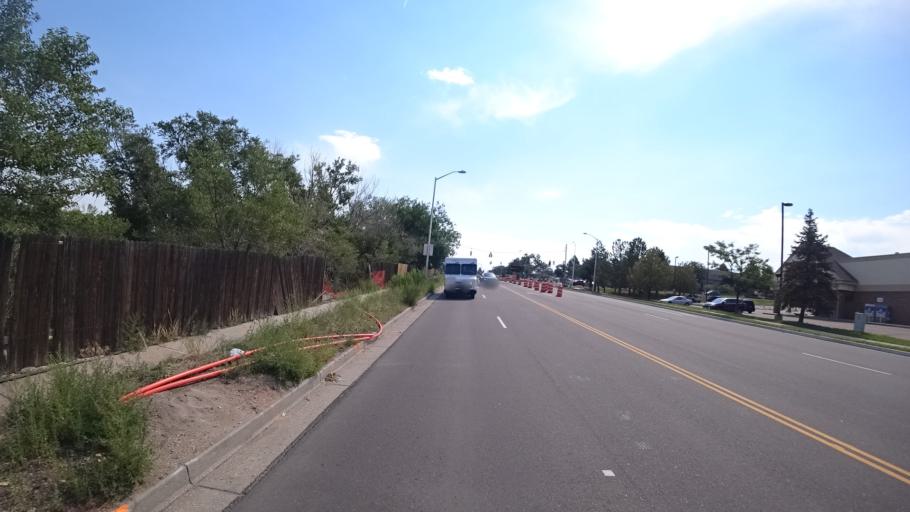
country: US
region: Colorado
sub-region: El Paso County
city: Colorado Springs
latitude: 38.9259
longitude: -104.7763
